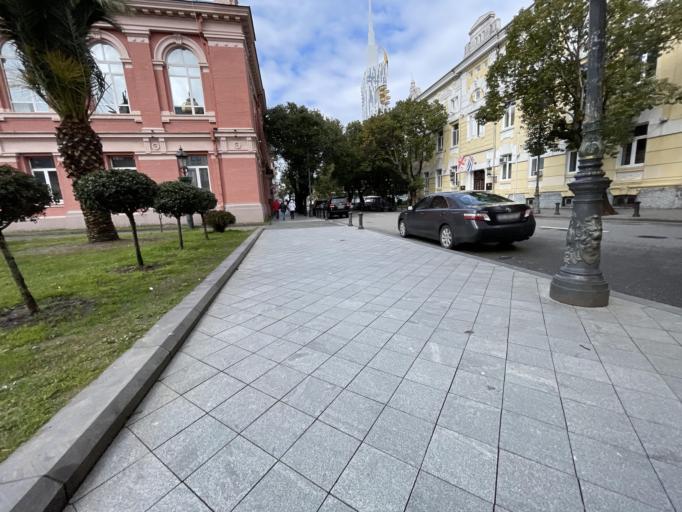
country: GE
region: Ajaria
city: Batumi
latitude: 41.6514
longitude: 41.6373
